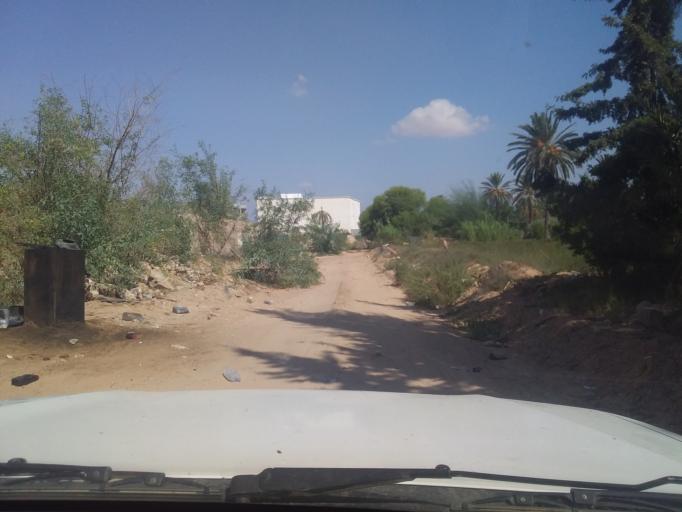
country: TN
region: Qabis
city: Gabes
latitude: 33.6274
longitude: 10.2822
